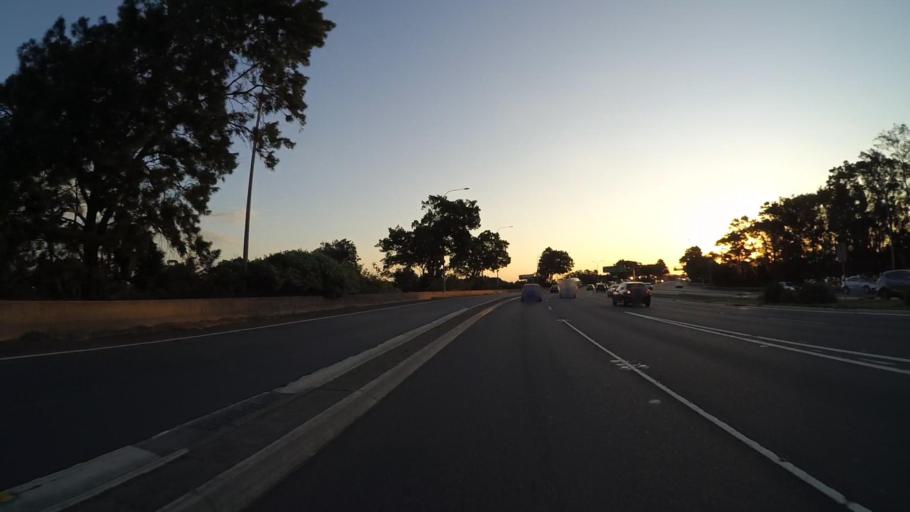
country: AU
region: New South Wales
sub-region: Botany Bay
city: Botany
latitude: -33.9433
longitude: 151.1919
